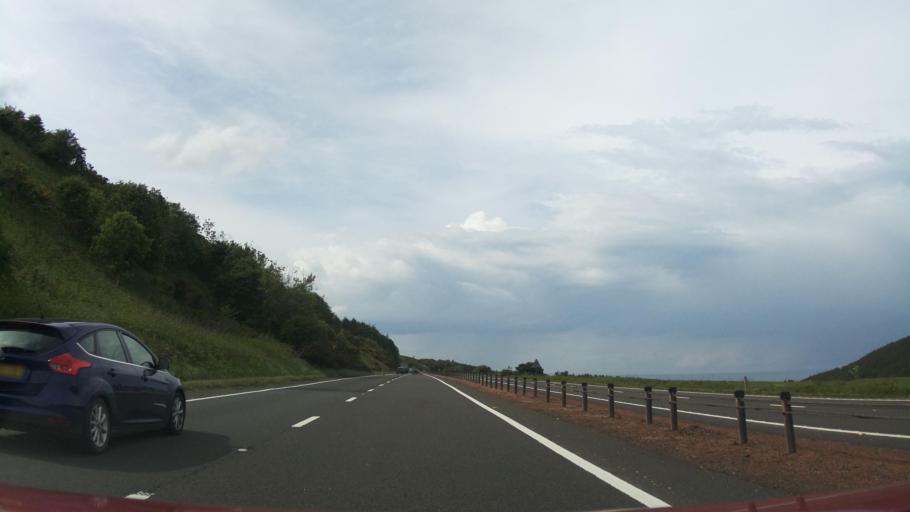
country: GB
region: Scotland
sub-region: The Scottish Borders
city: Duns
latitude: 55.9081
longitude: -2.3345
